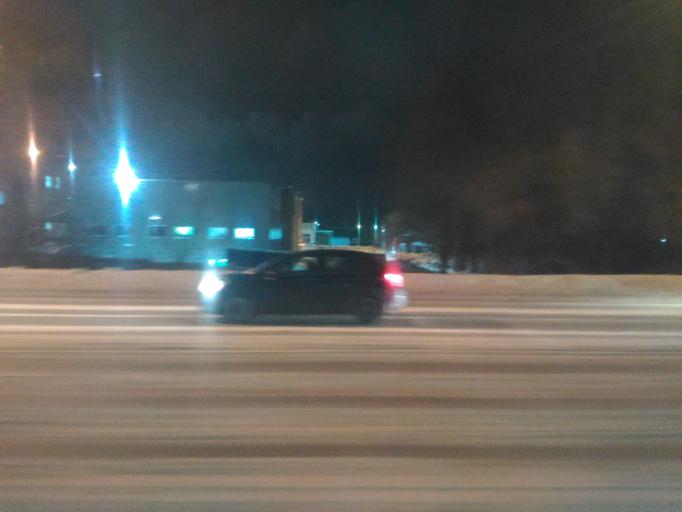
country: RU
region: Ulyanovsk
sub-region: Ulyanovskiy Rayon
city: Ulyanovsk
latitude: 54.3228
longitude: 48.3569
